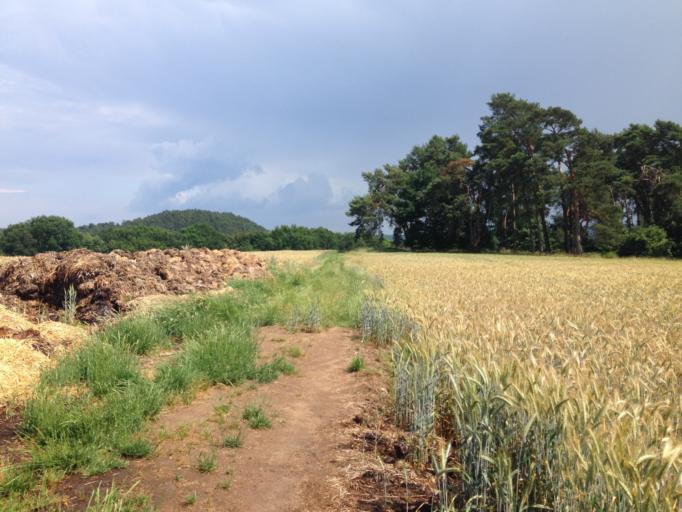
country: DE
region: Hesse
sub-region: Regierungsbezirk Giessen
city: Marburg an der Lahn
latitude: 50.8520
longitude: 8.7478
